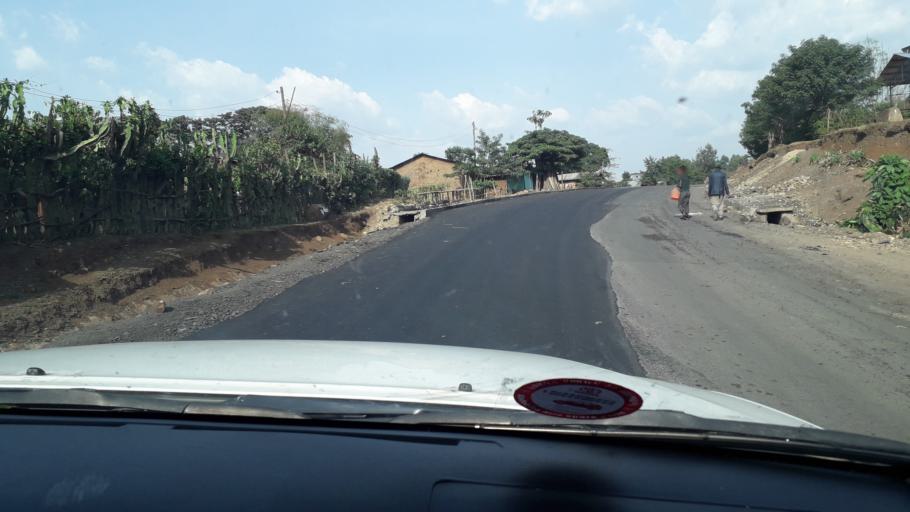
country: ET
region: Southern Nations, Nationalities, and People's Region
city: Mizan Teferi
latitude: 6.9333
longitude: 35.4925
